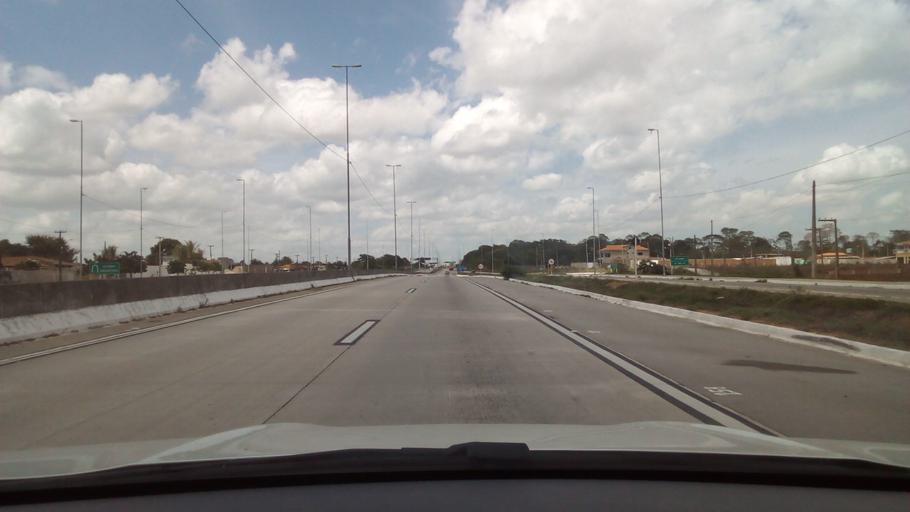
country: BR
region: Paraiba
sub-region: Mamanguape
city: Mamanguape
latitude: -6.8272
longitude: -35.1378
